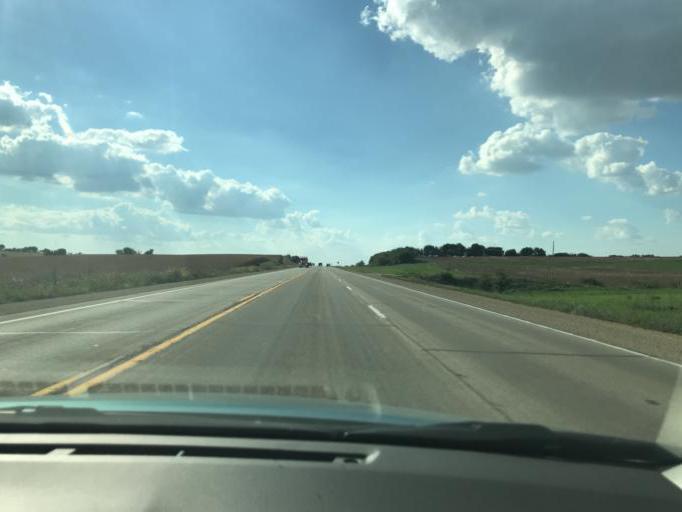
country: US
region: Wisconsin
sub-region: Green County
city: Brodhead
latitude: 42.5883
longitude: -89.4447
